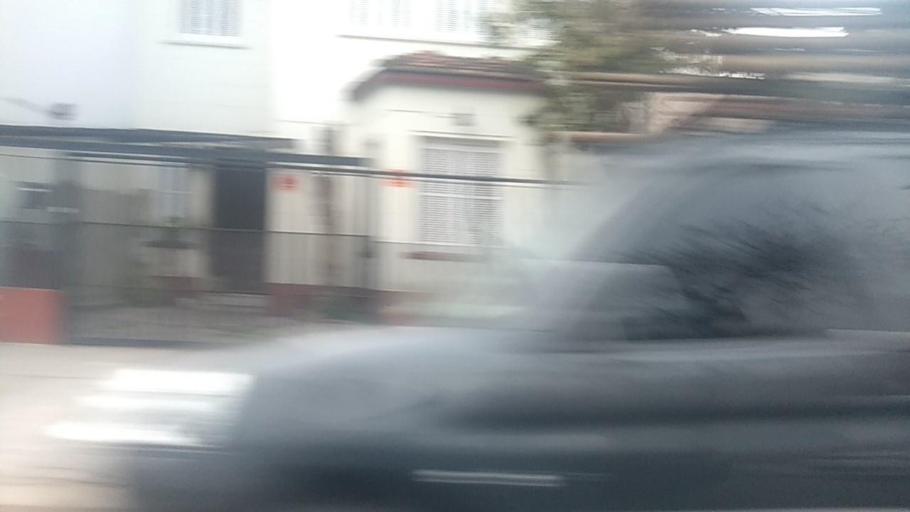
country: AR
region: Buenos Aires F.D.
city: Villa Santa Rita
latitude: -34.6027
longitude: -58.4994
